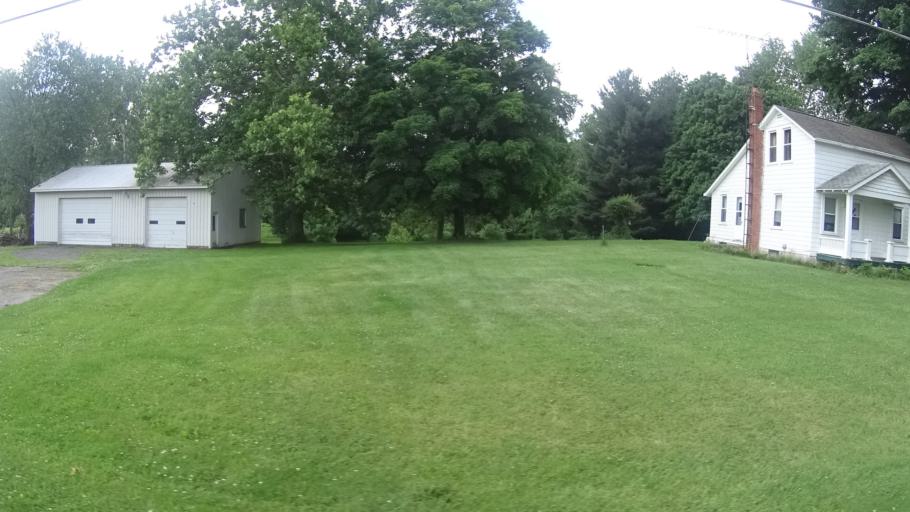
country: US
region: Ohio
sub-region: Huron County
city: Wakeman
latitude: 41.3231
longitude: -82.4222
